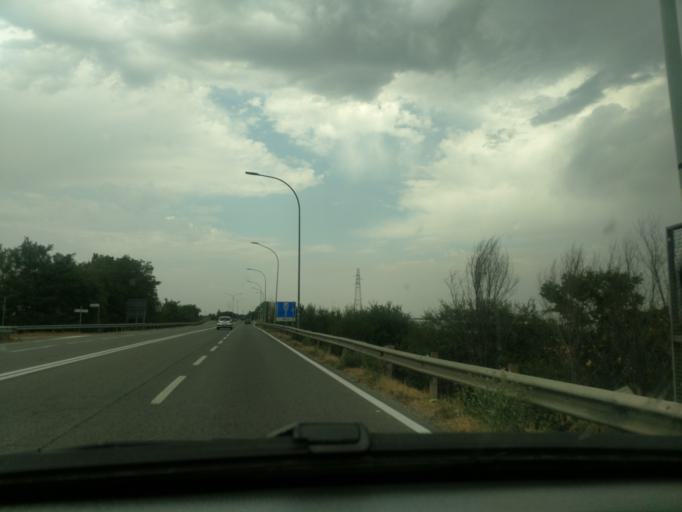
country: IT
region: Emilia-Romagna
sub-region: Provincia di Bologna
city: Calderara di Reno
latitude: 44.5272
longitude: 11.2643
